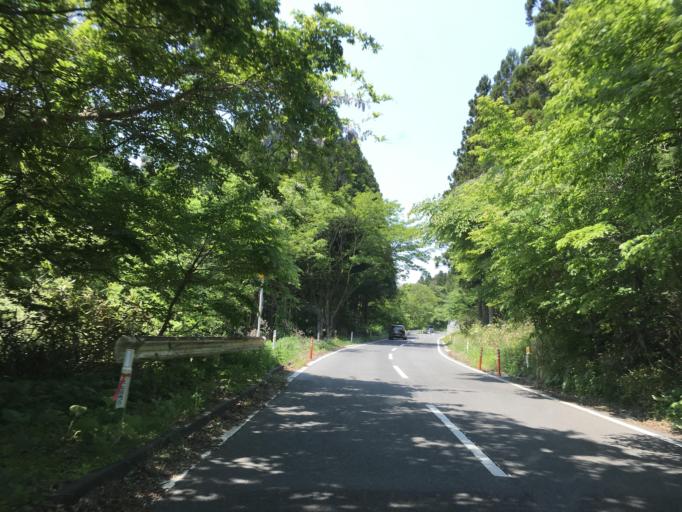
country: JP
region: Iwate
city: Ofunato
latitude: 38.8525
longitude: 141.4947
